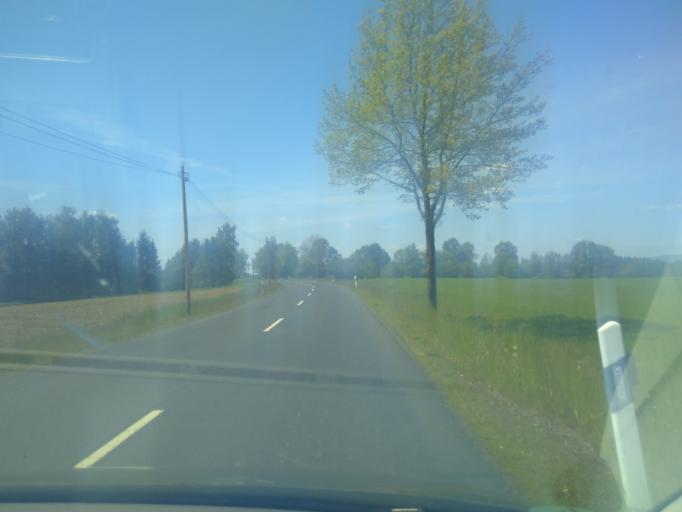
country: DE
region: Bavaria
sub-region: Upper Palatinate
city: Schwarzenbach
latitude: 49.8163
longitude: 12.3874
